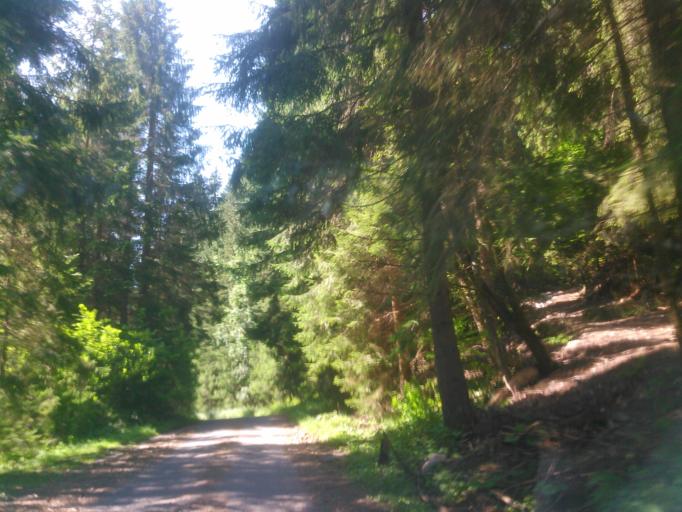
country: SK
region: Zilinsky
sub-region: Okres Liptovsky Mikulas
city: Liptovsky Mikulas
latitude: 48.9930
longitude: 19.5034
